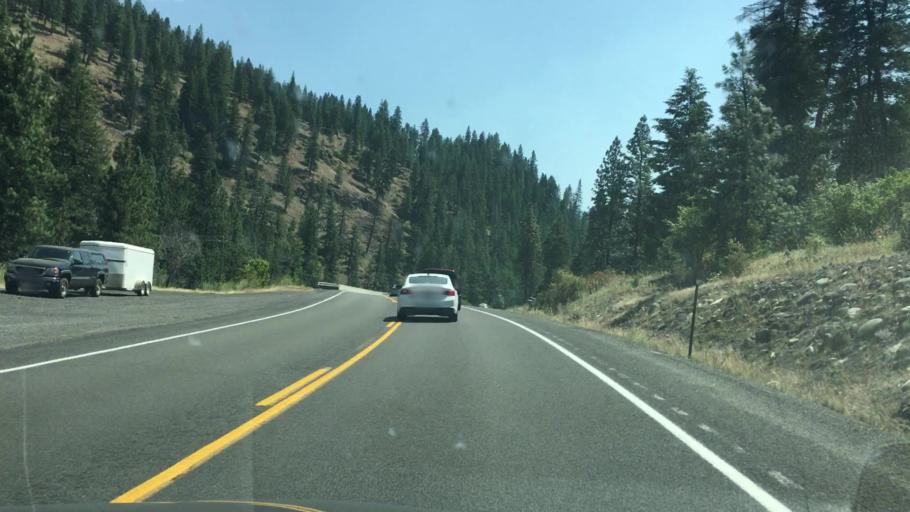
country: US
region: Idaho
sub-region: Valley County
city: McCall
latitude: 45.2044
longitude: -116.3125
